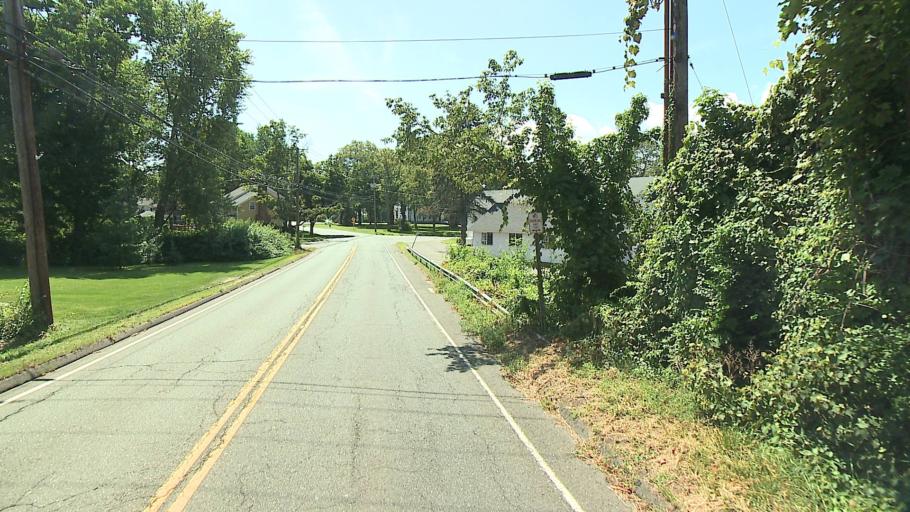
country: US
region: Connecticut
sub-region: Fairfield County
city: Trumbull
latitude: 41.3336
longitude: -73.2064
